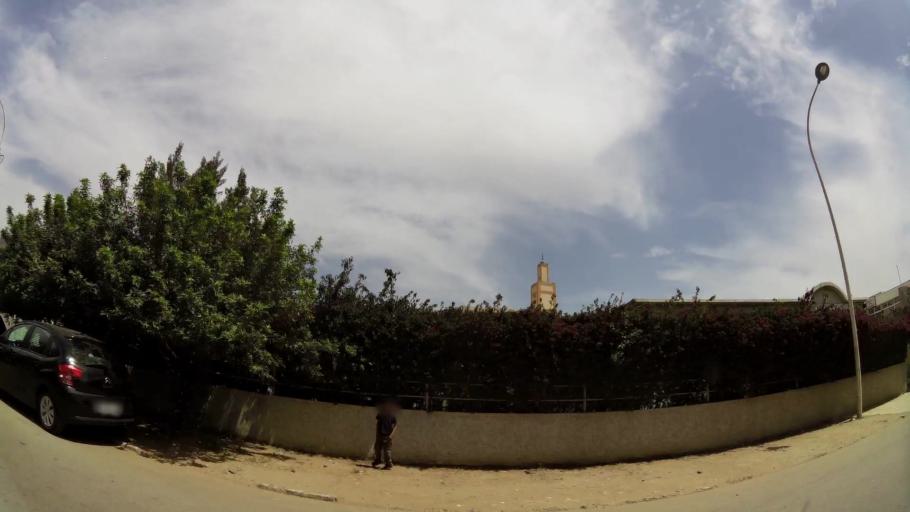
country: MA
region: Rabat-Sale-Zemmour-Zaer
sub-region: Khemisset
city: Khemisset
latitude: 33.8169
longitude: -6.0708
